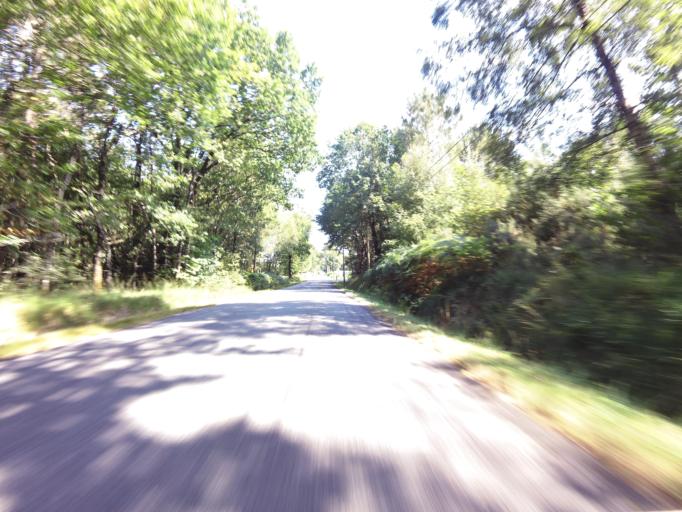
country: FR
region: Brittany
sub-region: Departement du Morbihan
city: Limerzel
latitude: 47.6541
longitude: -2.3889
